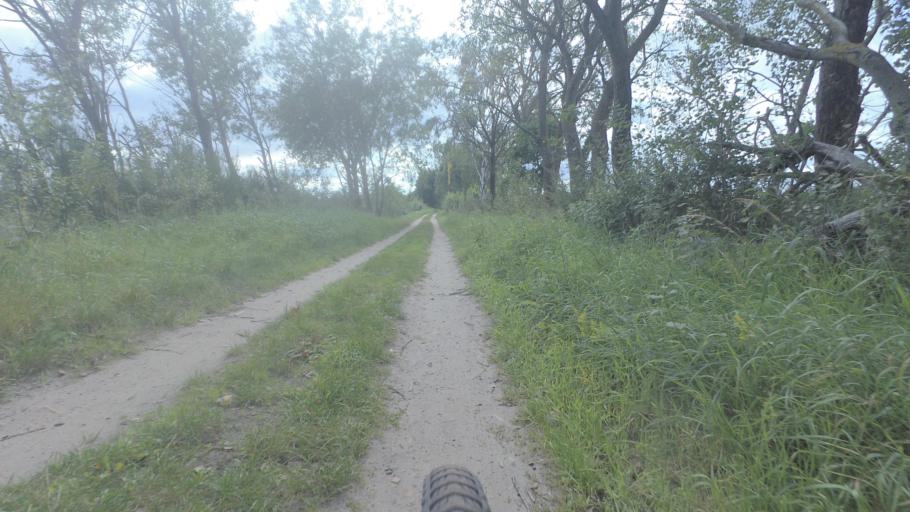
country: DE
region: Brandenburg
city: Ludwigsfelde
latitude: 52.3237
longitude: 13.2074
